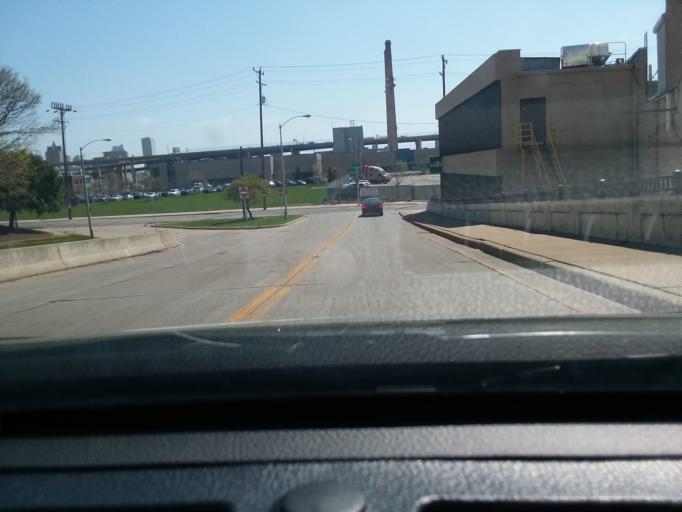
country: US
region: Wisconsin
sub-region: Milwaukee County
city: Milwaukee
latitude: 43.0305
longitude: -87.9314
